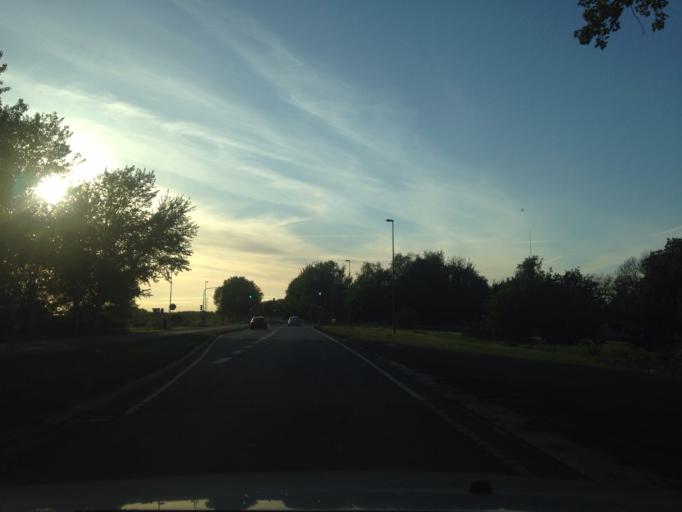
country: DK
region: Zealand
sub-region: Greve Kommune
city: Tune
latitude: 55.5980
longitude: 12.2297
